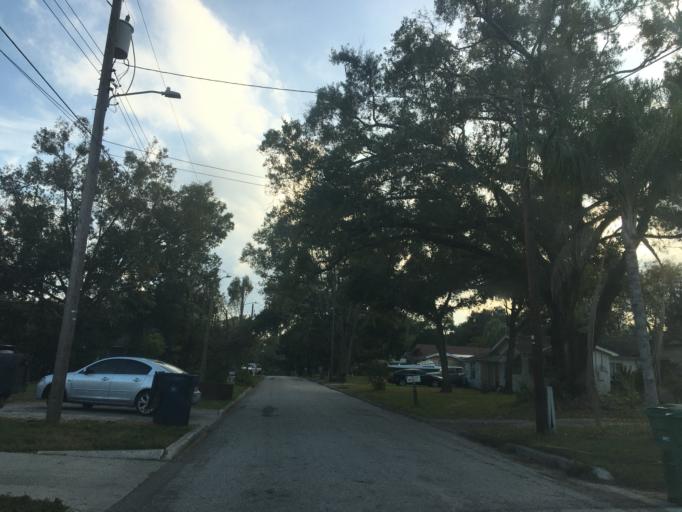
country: US
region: Florida
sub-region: Hillsborough County
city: Temple Terrace
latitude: 28.0316
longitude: -82.4248
